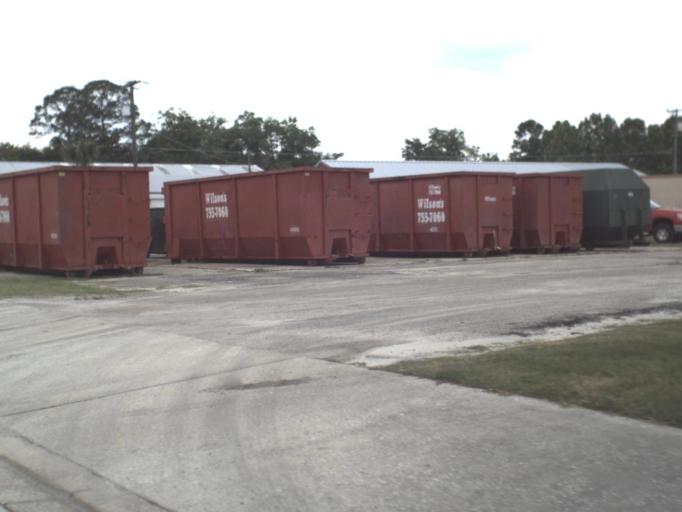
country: US
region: Florida
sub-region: Columbia County
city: Watertown
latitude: 30.1824
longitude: -82.6168
